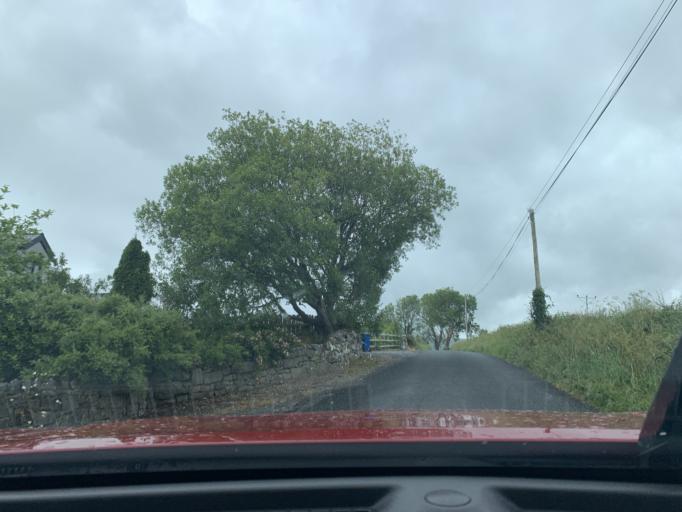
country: IE
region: Connaught
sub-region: Sligo
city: Sligo
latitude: 54.3053
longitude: -8.4562
